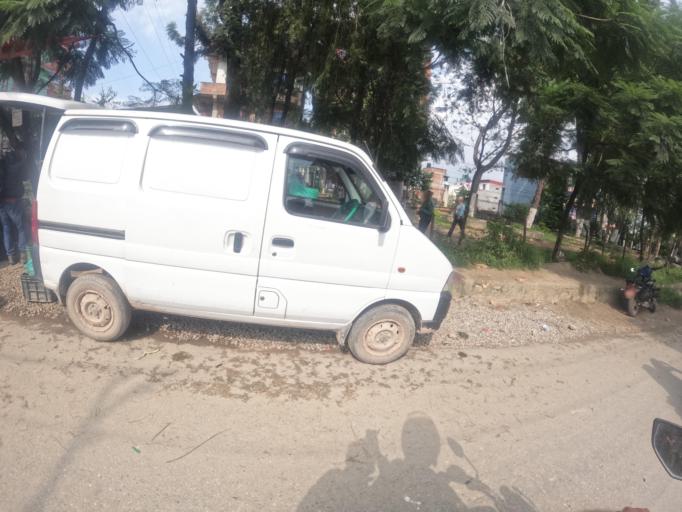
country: NP
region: Central Region
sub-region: Bagmati Zone
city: Bhaktapur
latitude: 27.6673
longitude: 85.3861
